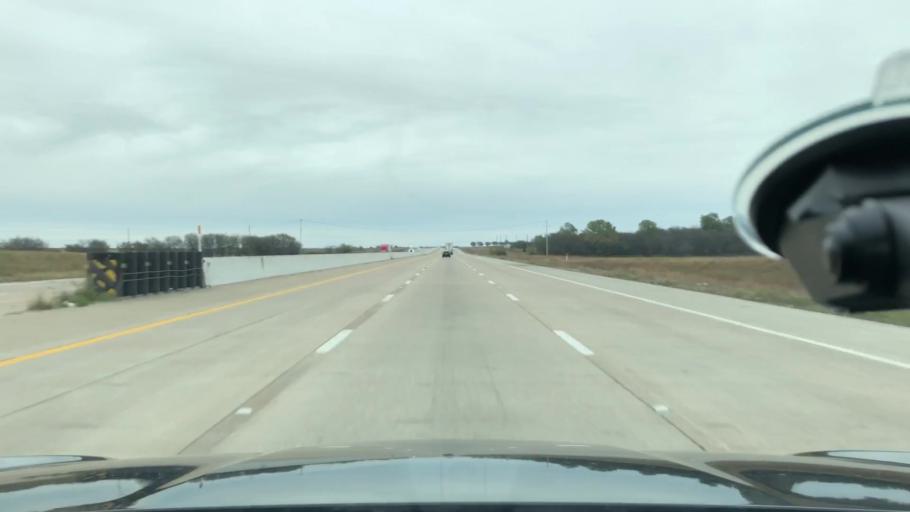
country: US
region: Texas
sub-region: Ellis County
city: Italy
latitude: 32.1555
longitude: -96.9276
